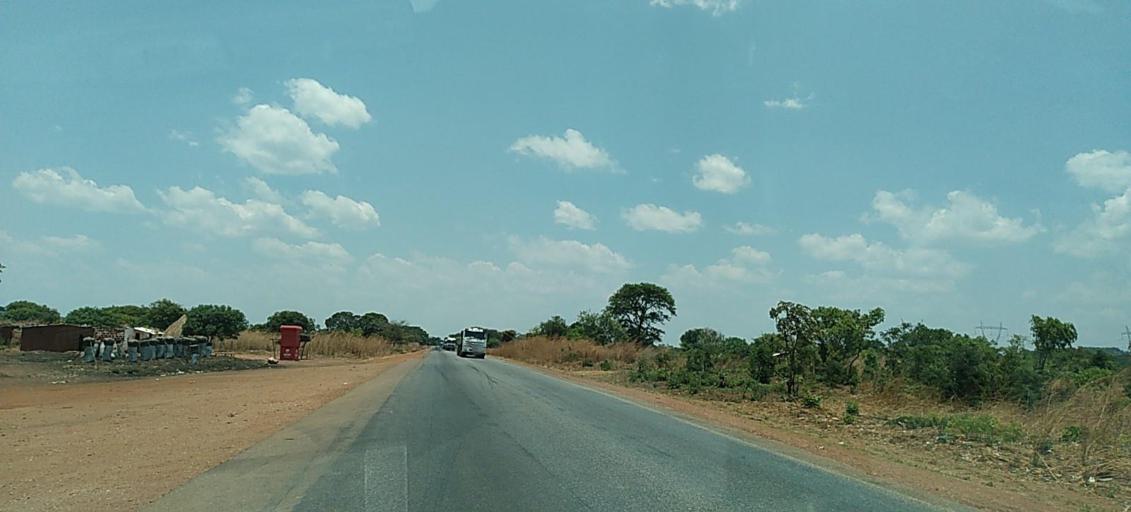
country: ZM
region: Central
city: Kapiri Mposhi
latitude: -13.7075
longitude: 28.6306
